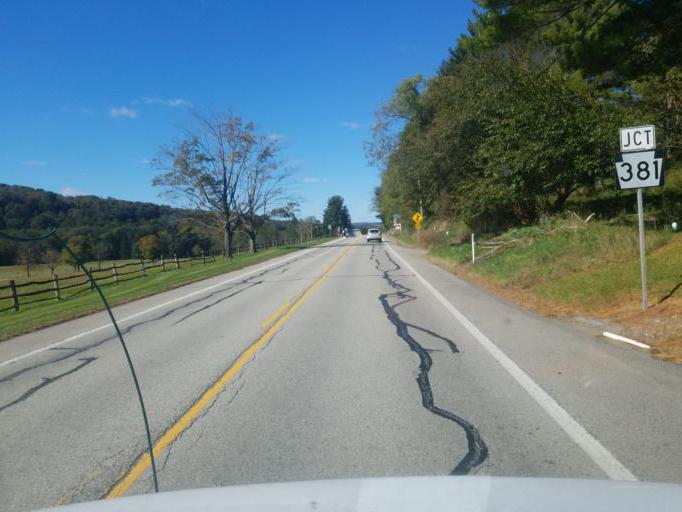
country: US
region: Pennsylvania
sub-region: Westmoreland County
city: Ligonier
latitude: 40.2205
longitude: -79.2130
